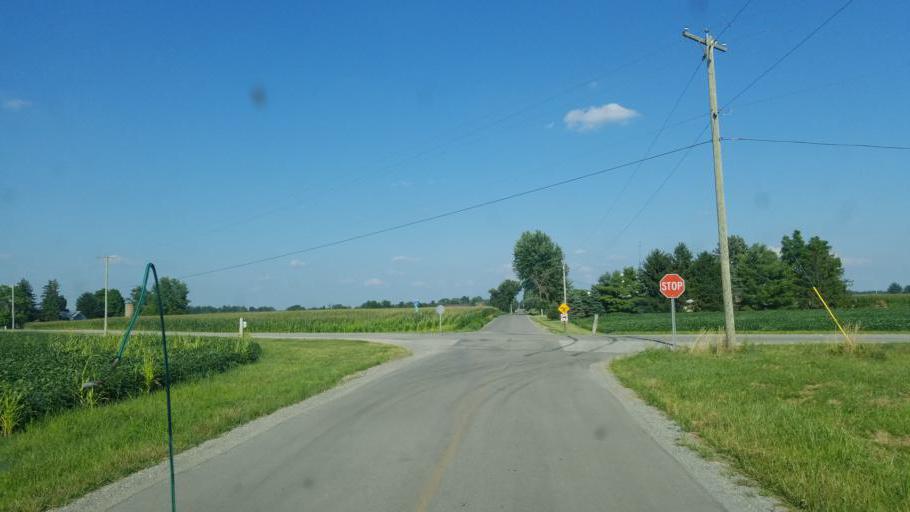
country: US
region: Ohio
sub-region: Wyandot County
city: Upper Sandusky
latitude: 40.7888
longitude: -83.2949
